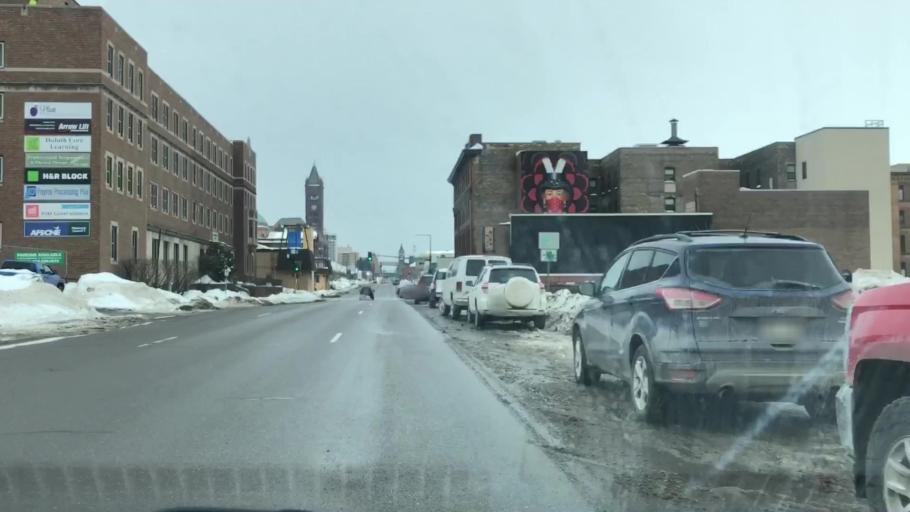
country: US
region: Minnesota
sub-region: Saint Louis County
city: Duluth
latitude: 46.7856
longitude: -92.1038
